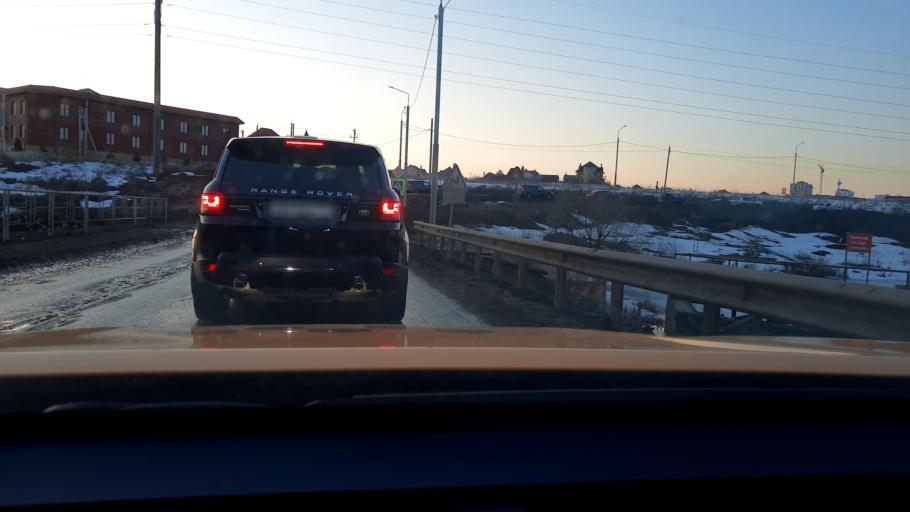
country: RU
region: Moskovskaya
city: Vidnoye
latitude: 55.5234
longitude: 37.7191
